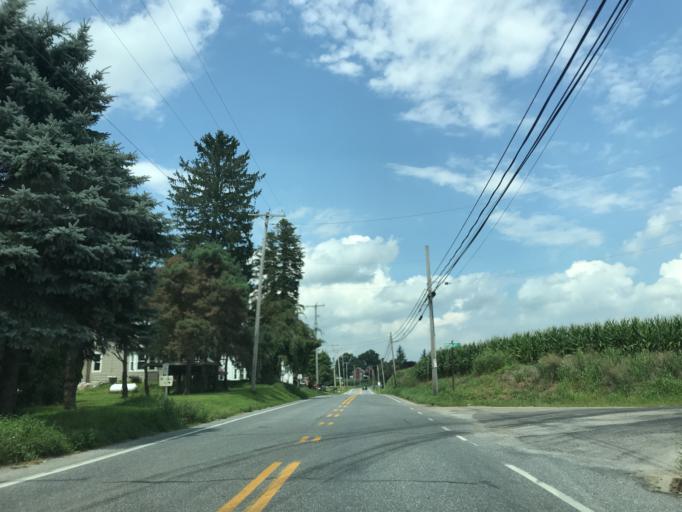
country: US
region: Pennsylvania
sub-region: York County
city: Red Lion
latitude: 39.8435
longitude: -76.6207
